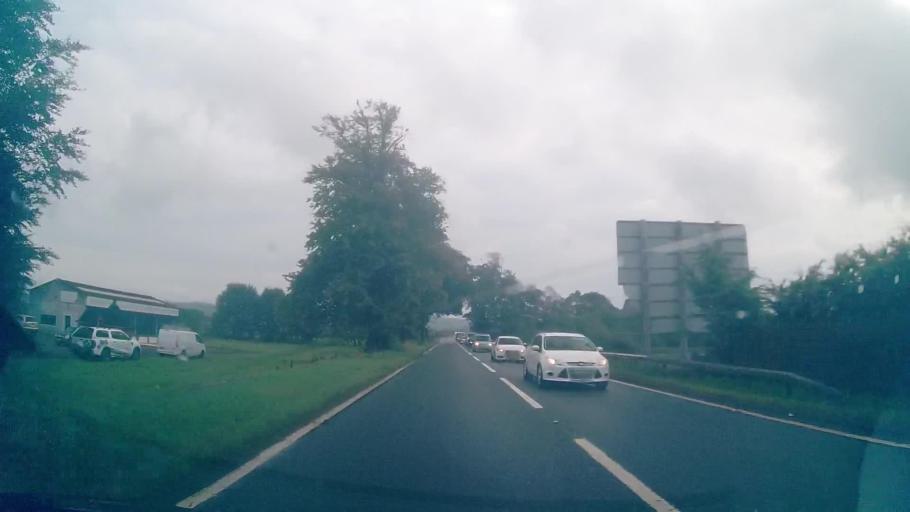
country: GB
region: Scotland
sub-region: Dumfries and Galloway
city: Locharbriggs
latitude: 55.0686
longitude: -3.5504
